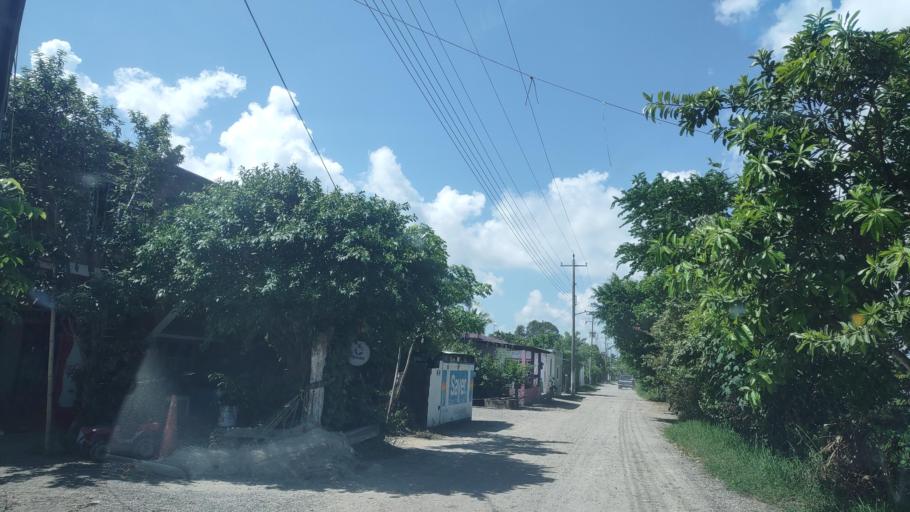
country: MX
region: Veracruz
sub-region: Ozuluama de Mascarenas
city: Cucharas
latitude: 21.6190
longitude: -97.6532
